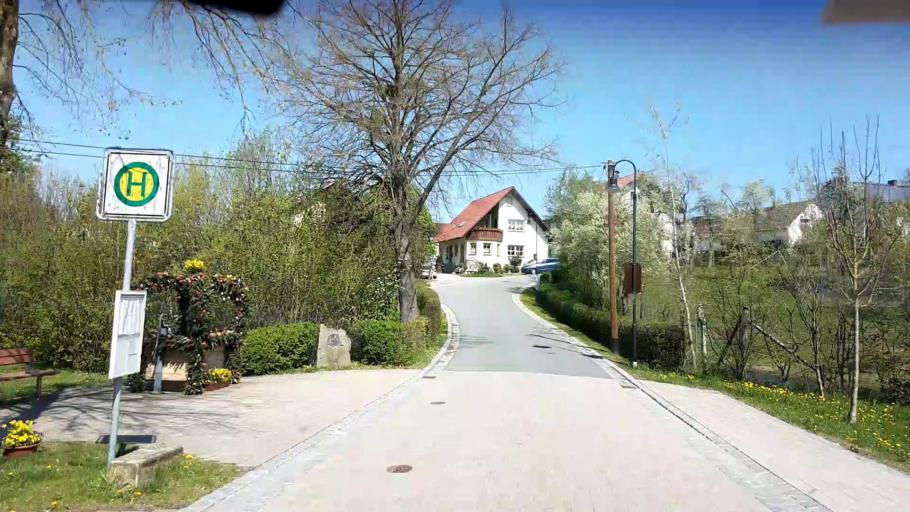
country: DE
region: Bavaria
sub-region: Upper Franconia
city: Zapfendorf
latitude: 50.0011
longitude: 10.9679
